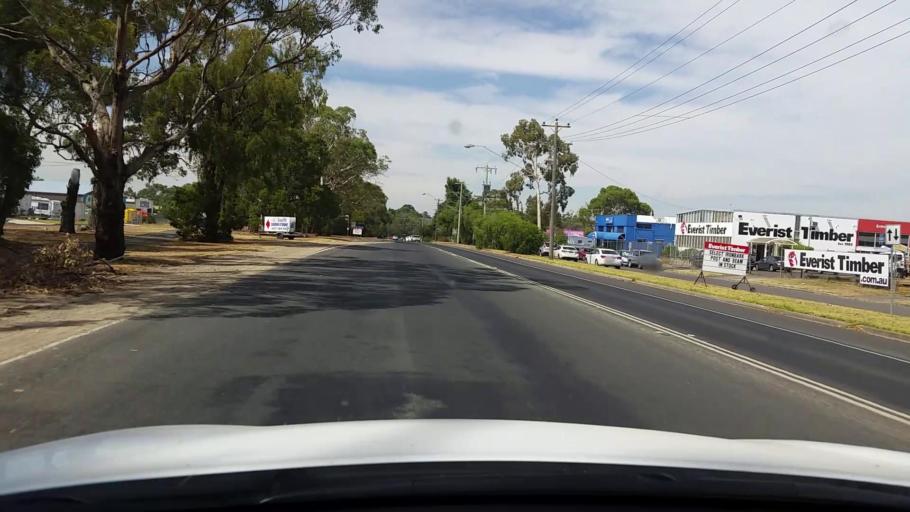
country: AU
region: Victoria
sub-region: Mornington Peninsula
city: Hastings
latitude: -38.3130
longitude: 145.1836
